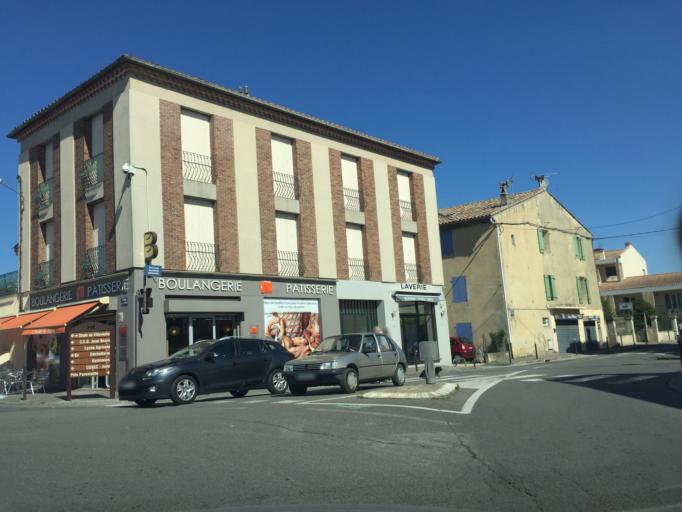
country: FR
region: Provence-Alpes-Cote d'Azur
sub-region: Departement du Vaucluse
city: L'Isle-sur-la-Sorgue
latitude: 43.9218
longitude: 5.0481
